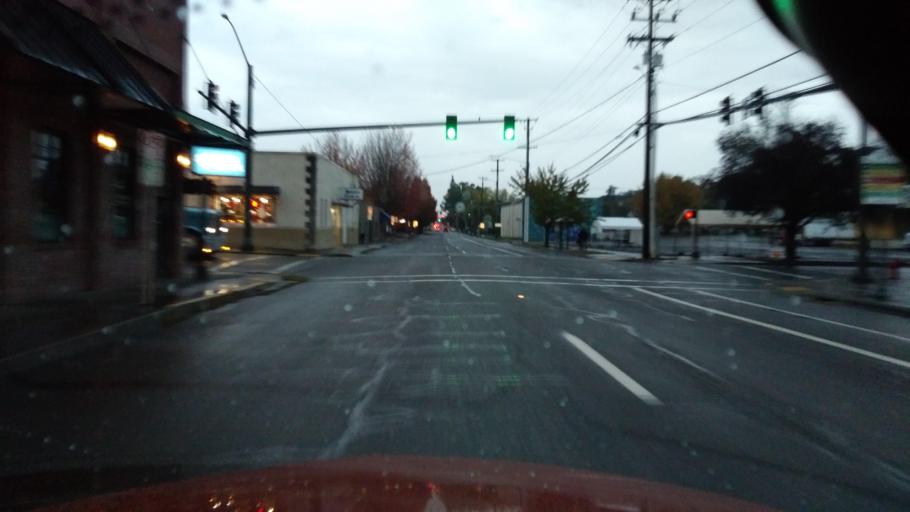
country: US
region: Oregon
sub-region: Washington County
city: Forest Grove
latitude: 45.5184
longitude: -123.1126
